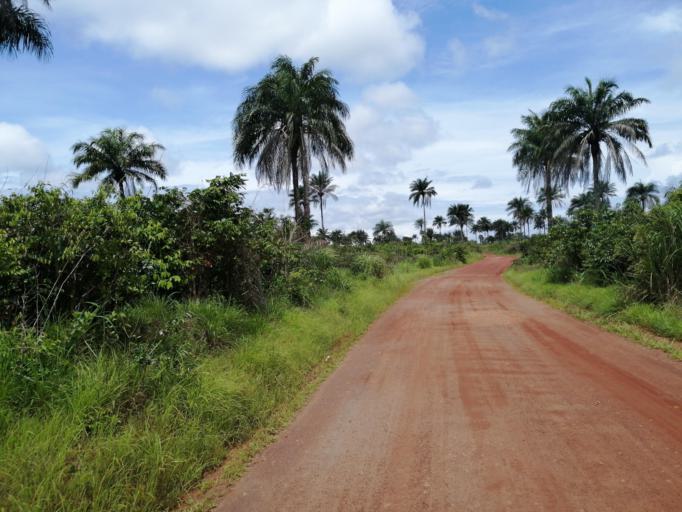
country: SL
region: Northern Province
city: Pepel
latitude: 8.6511
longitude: -13.0091
